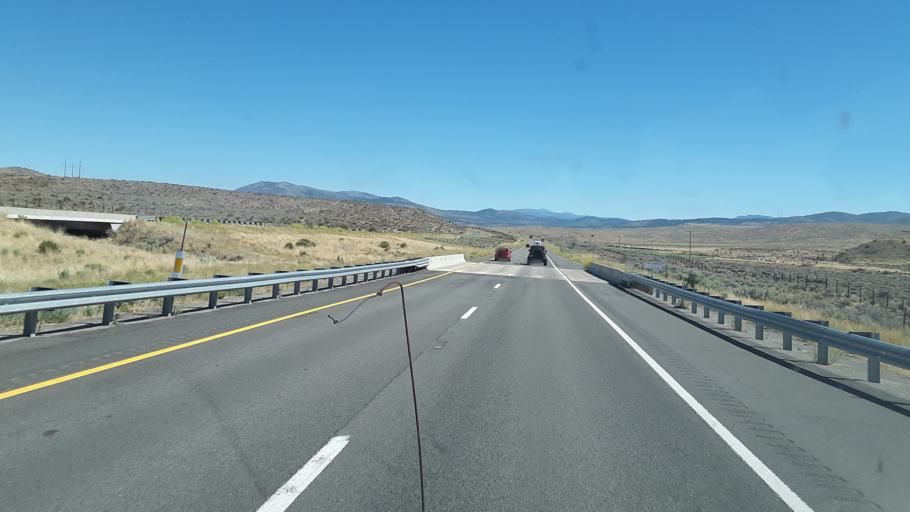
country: US
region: Nevada
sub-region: Washoe County
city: Cold Springs
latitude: 39.7108
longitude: -120.0359
